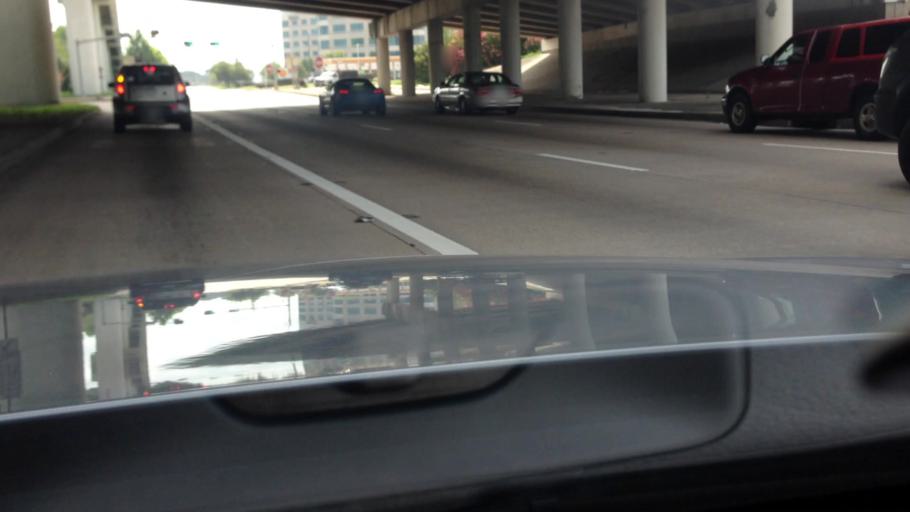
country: US
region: Texas
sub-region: Harris County
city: Hudson
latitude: 29.9365
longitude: -95.5159
